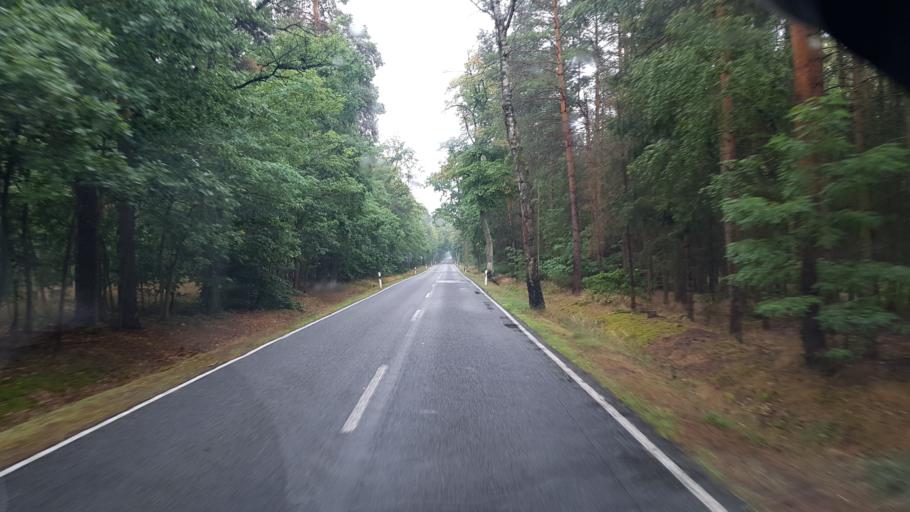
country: DE
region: Brandenburg
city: Dahme
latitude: 51.8410
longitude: 13.4131
